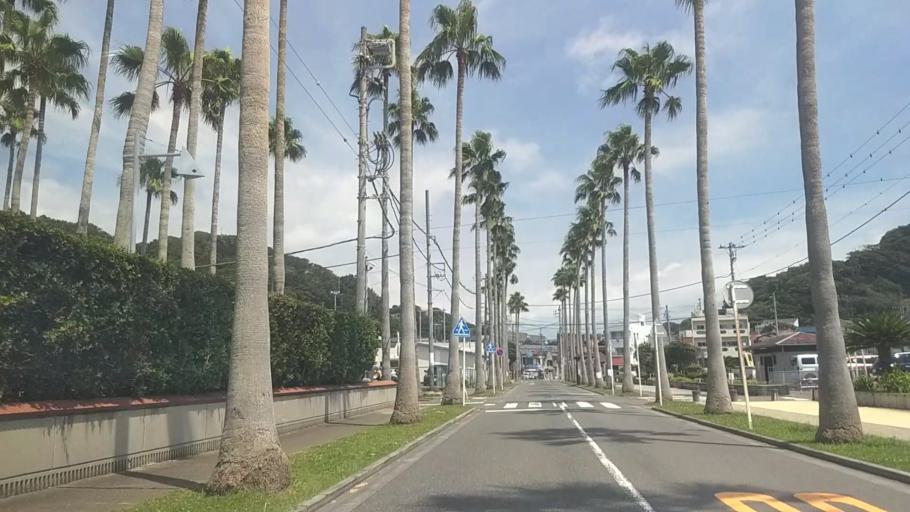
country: JP
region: Kanagawa
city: Kamakura
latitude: 35.2968
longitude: 139.5547
